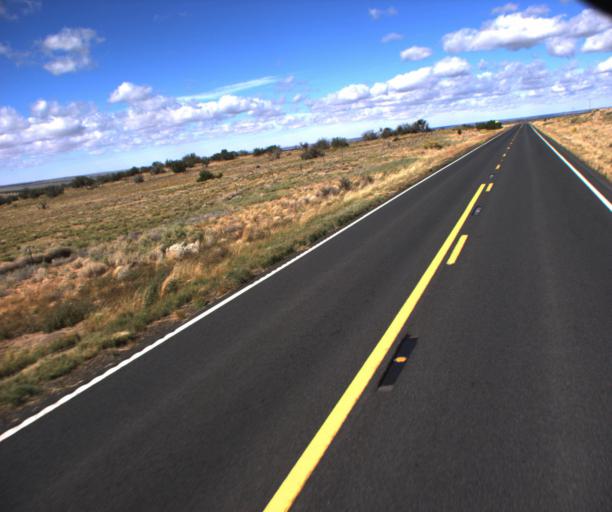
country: US
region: Arizona
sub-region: Apache County
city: Houck
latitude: 35.0790
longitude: -109.3006
